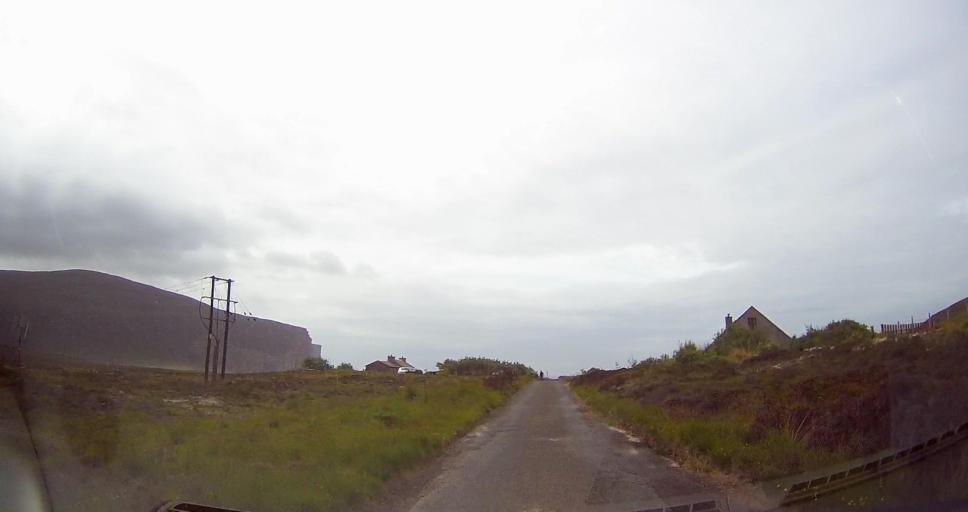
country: GB
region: Scotland
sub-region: Orkney Islands
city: Stromness
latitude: 58.8772
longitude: -3.3860
